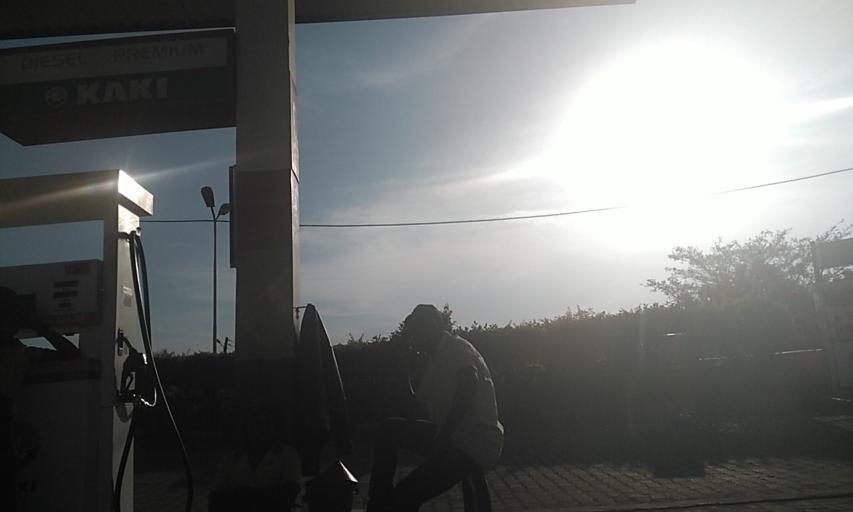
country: UG
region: Central Region
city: Kampala Central Division
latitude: 0.3111
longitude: 32.5569
